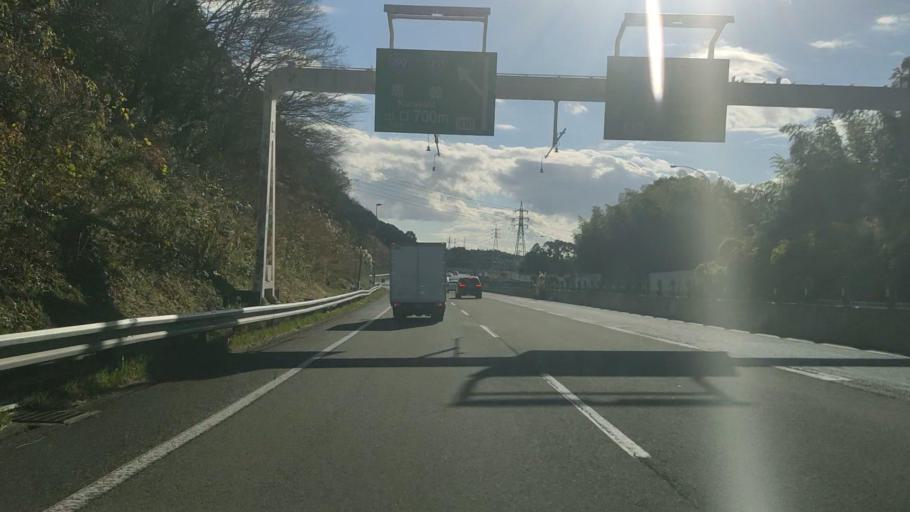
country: JP
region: Fukuoka
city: Kitakyushu
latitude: 33.8485
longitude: 130.7670
